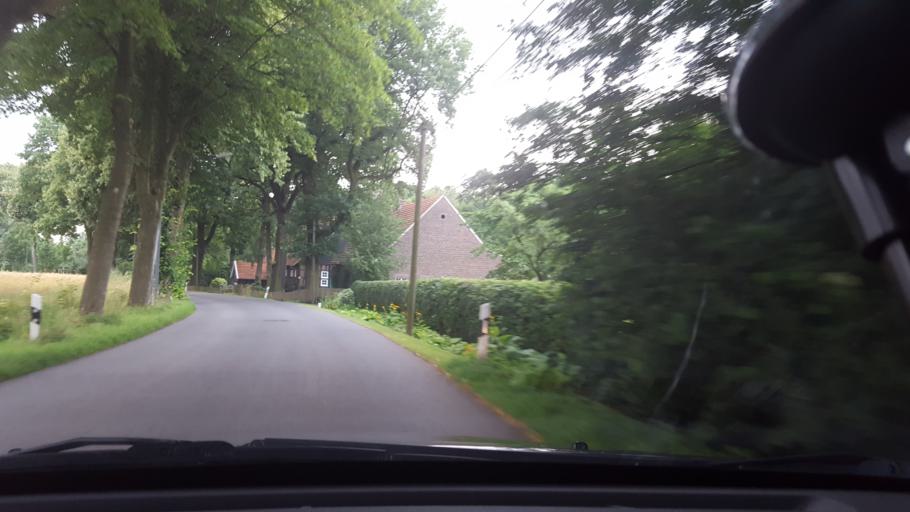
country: DE
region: North Rhine-Westphalia
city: Herten
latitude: 51.6270
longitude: 7.1420
